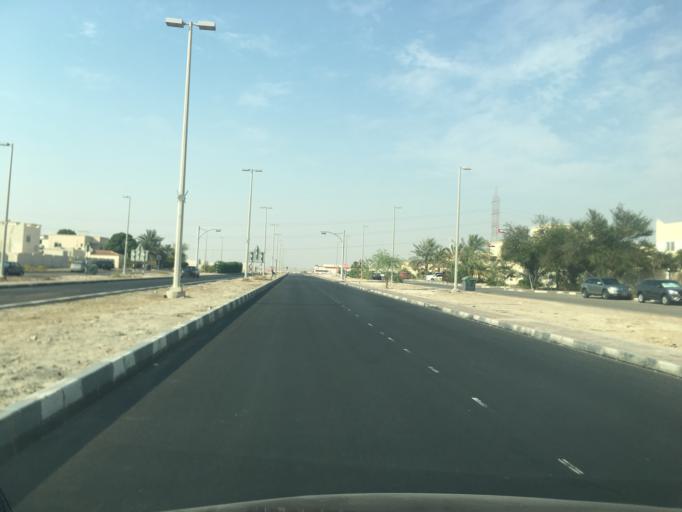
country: AE
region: Abu Dhabi
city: Abu Dhabi
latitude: 24.3011
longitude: 54.6496
